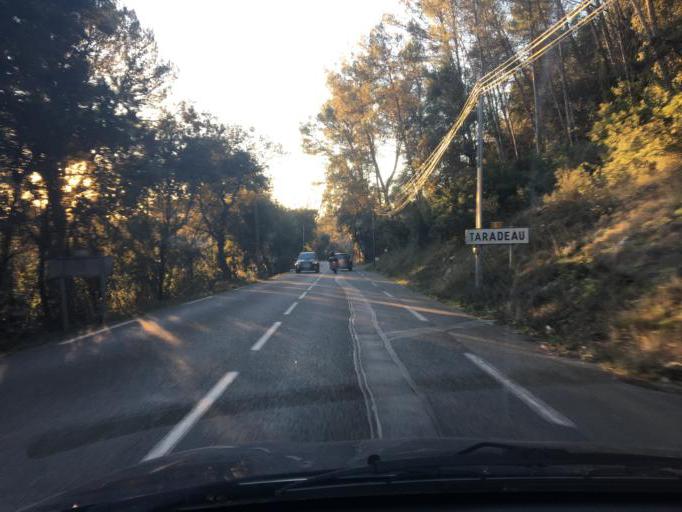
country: FR
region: Provence-Alpes-Cote d'Azur
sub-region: Departement du Var
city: Taradeau
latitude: 43.4565
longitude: 6.4210
